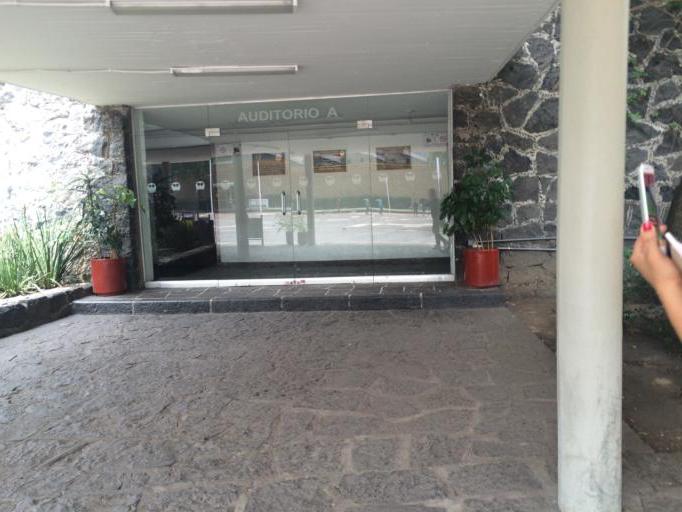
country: MX
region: Mexico City
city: Coyoacan
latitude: 19.3313
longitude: -99.1816
